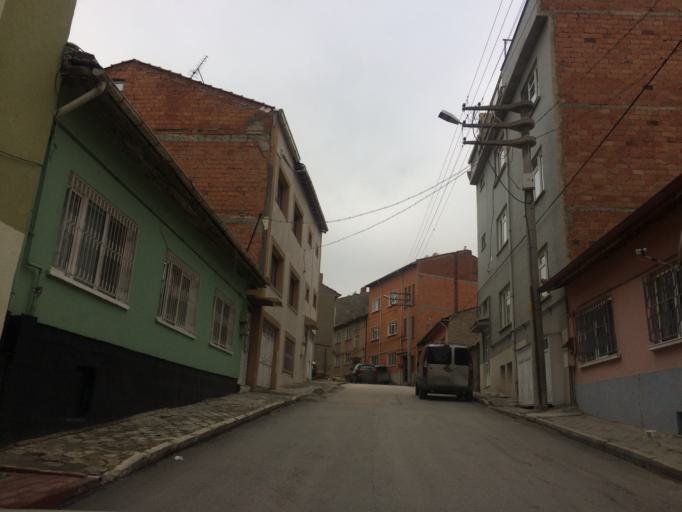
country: TR
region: Eskisehir
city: Eskisehir
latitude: 39.7917
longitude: 30.4798
